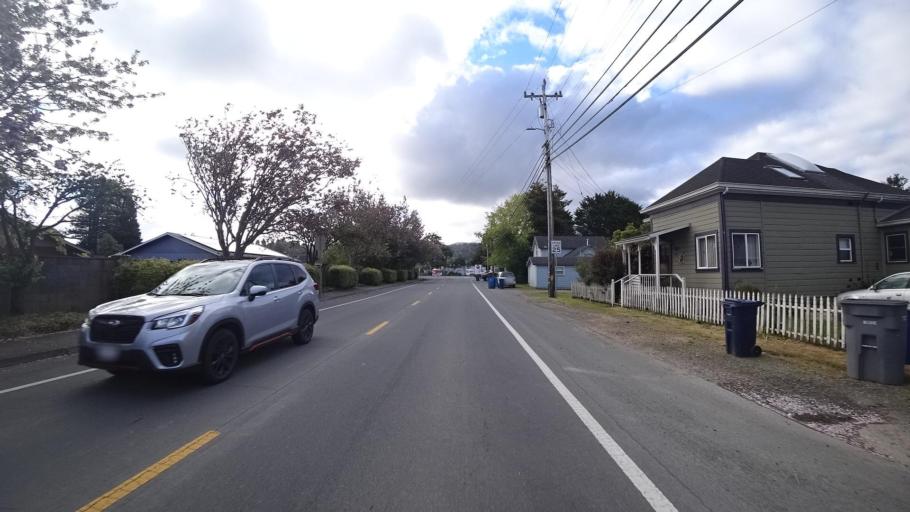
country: US
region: California
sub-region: Humboldt County
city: Arcata
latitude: 40.8907
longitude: -124.0887
